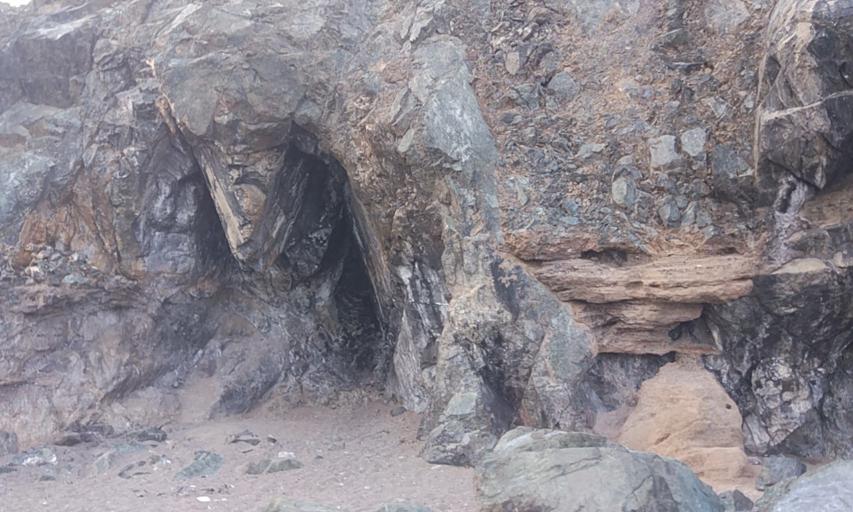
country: TR
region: Antalya
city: Tekirova
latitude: 36.4223
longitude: 30.4878
